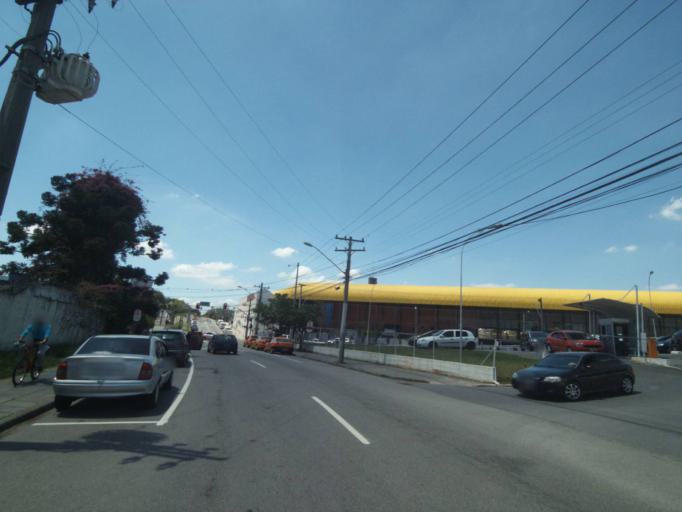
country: BR
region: Parana
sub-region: Curitiba
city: Curitiba
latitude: -25.3846
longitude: -49.2332
